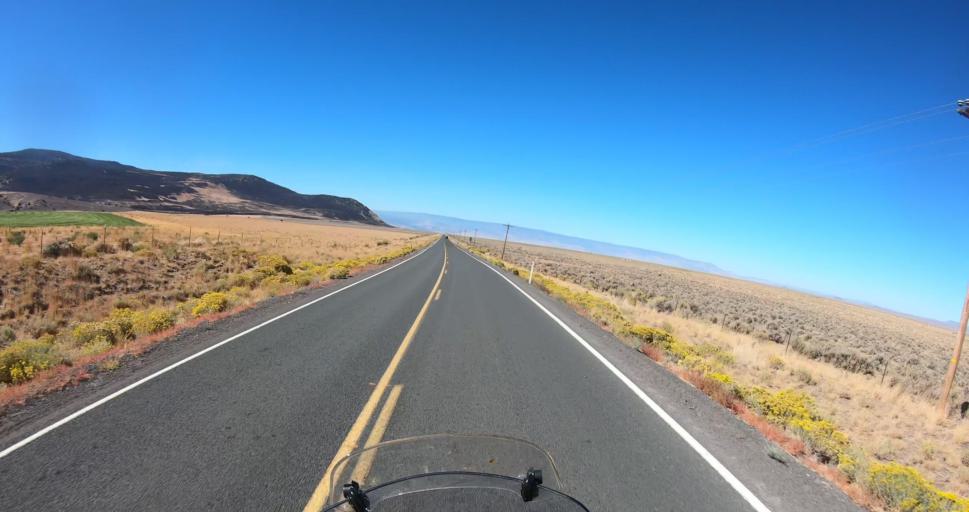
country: US
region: Oregon
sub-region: Lake County
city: Lakeview
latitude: 42.7064
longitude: -120.5520
